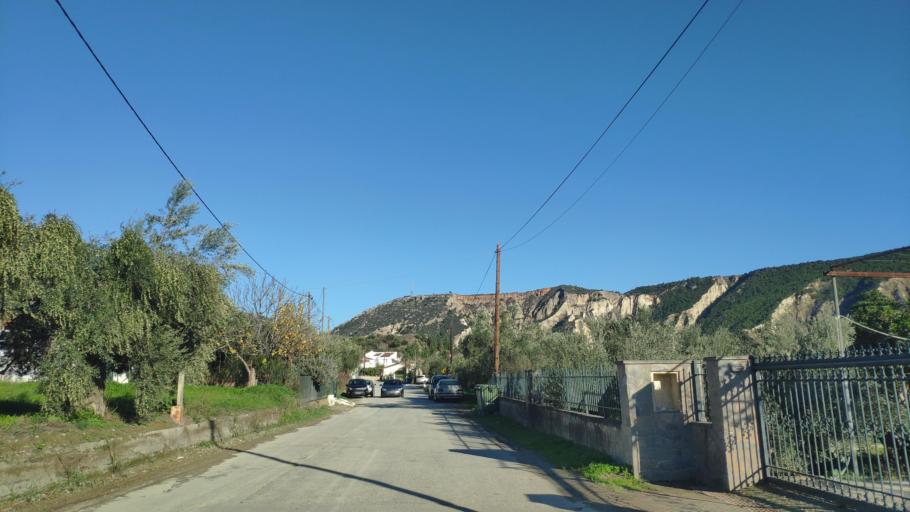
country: GR
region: Peloponnese
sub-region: Nomos Korinthias
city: Xylokastro
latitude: 38.0559
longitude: 22.6069
